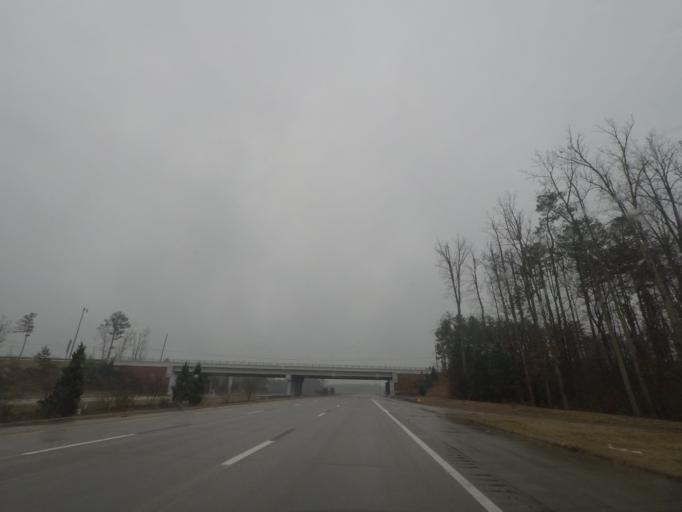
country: US
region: North Carolina
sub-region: Wake County
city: Green Level
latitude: 35.7842
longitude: -78.8868
